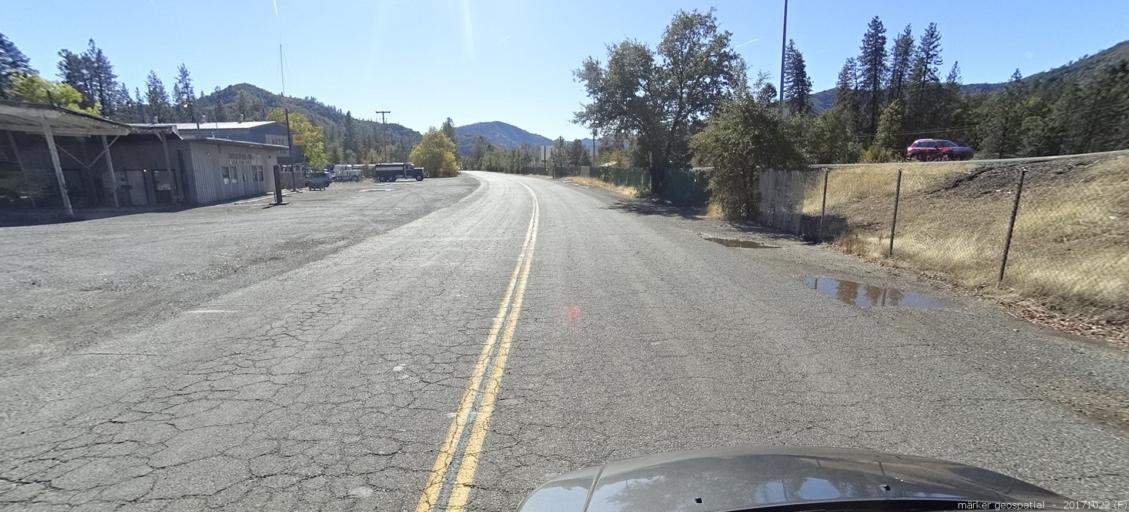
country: US
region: California
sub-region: Shasta County
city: Central Valley (historical)
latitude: 40.8902
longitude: -122.3829
